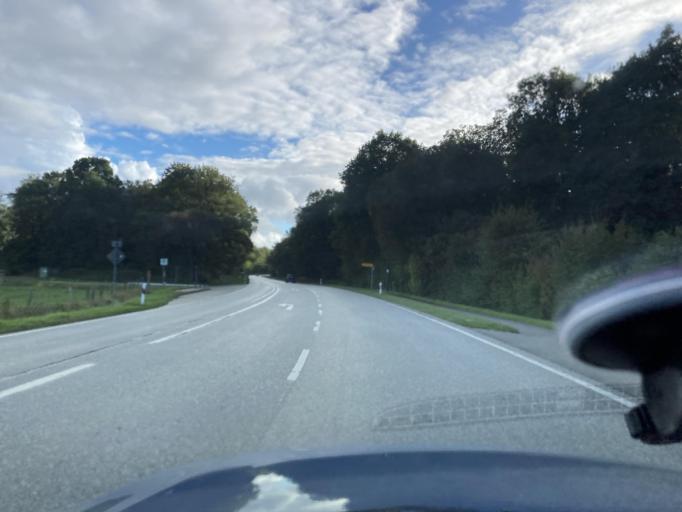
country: DE
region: Schleswig-Holstein
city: Fockbek
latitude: 54.2802
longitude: 9.5735
